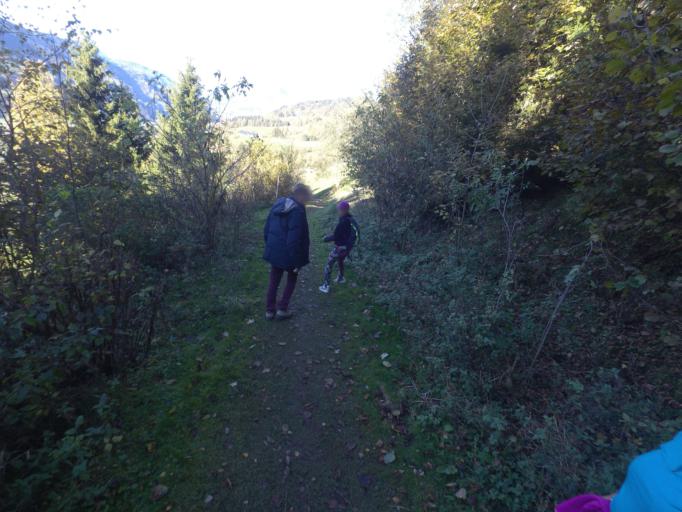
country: AT
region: Salzburg
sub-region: Politischer Bezirk Sankt Johann im Pongau
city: Sankt Johann im Pongau
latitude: 47.3426
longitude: 13.2202
